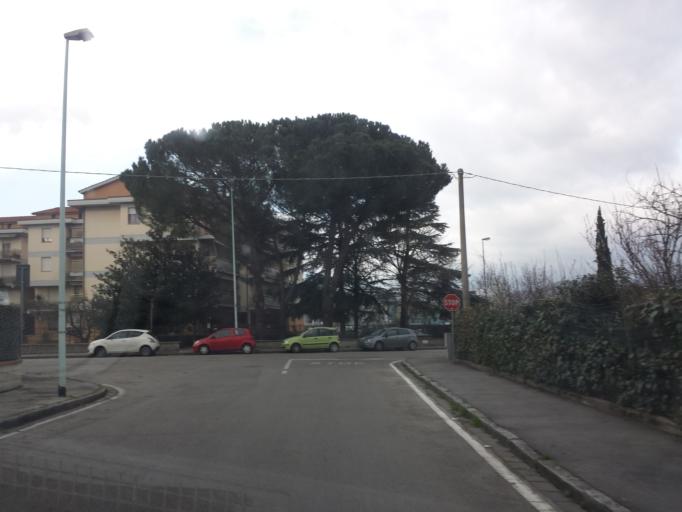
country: IT
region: Tuscany
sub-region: Provincia di Prato
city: Prato
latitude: 43.8872
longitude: 11.0614
